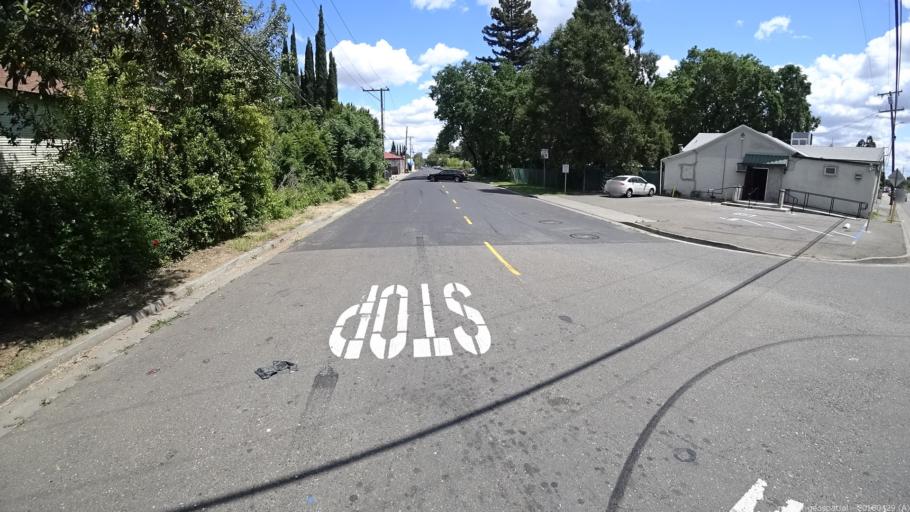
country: US
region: California
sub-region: Yolo County
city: West Sacramento
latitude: 38.5938
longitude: -121.5456
